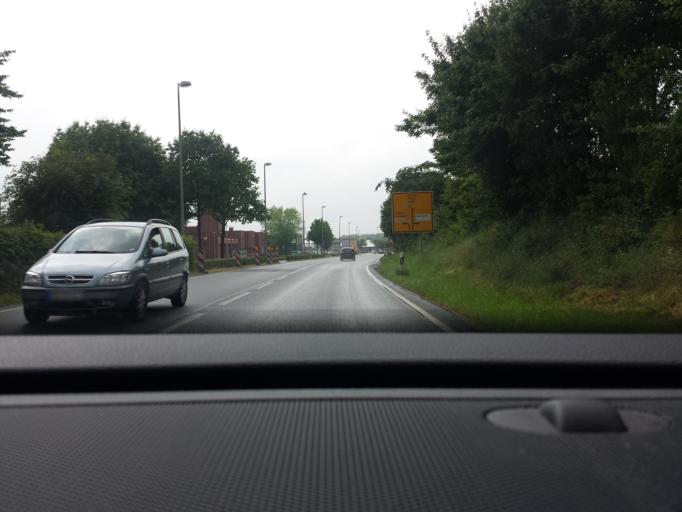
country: DE
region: North Rhine-Westphalia
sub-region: Regierungsbezirk Munster
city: Ahaus
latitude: 52.0715
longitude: 6.9996
